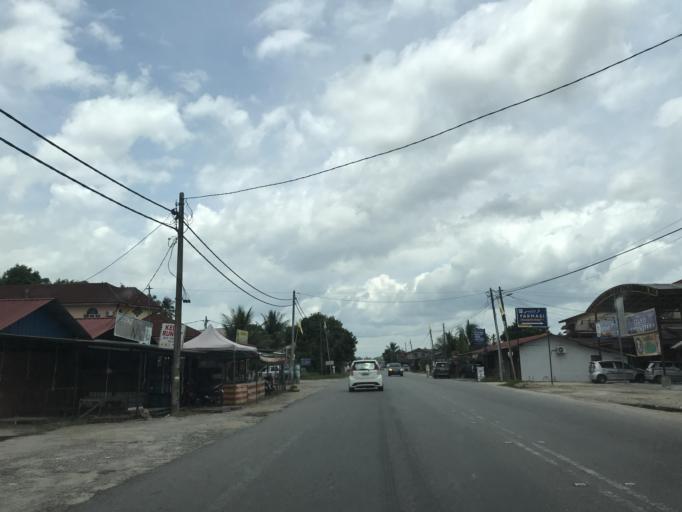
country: MY
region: Kelantan
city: Kota Bharu
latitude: 6.0722
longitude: 102.2077
